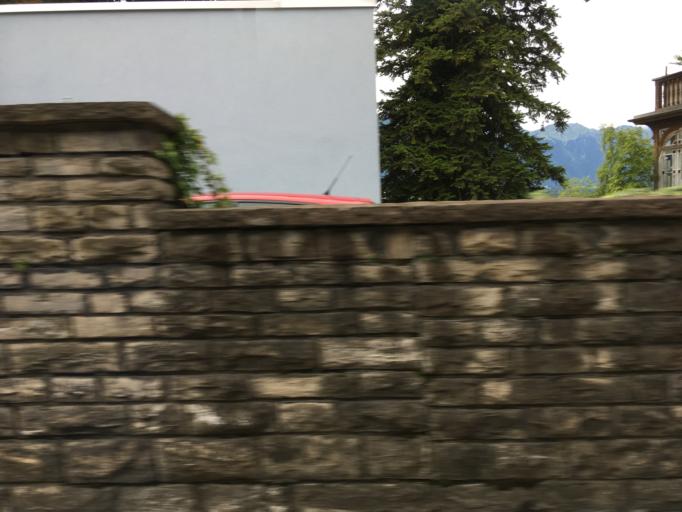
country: CH
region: Bern
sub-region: Thun District
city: Hilterfingen
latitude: 46.7351
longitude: 7.6585
